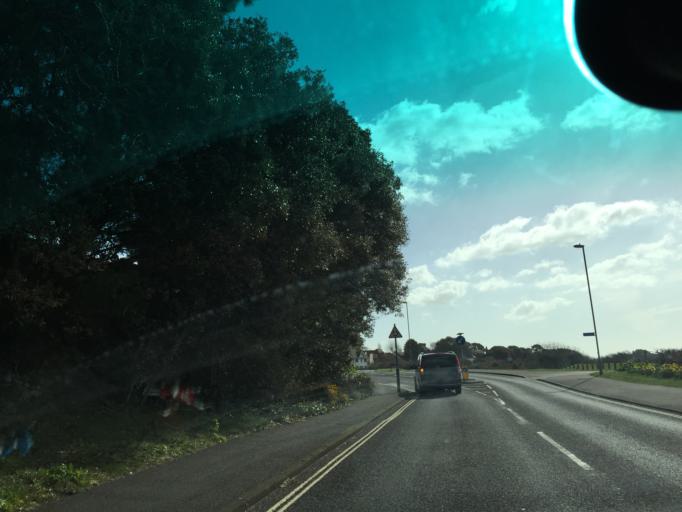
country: GB
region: England
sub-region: Hampshire
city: Gosport
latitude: 50.7825
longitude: -1.1496
